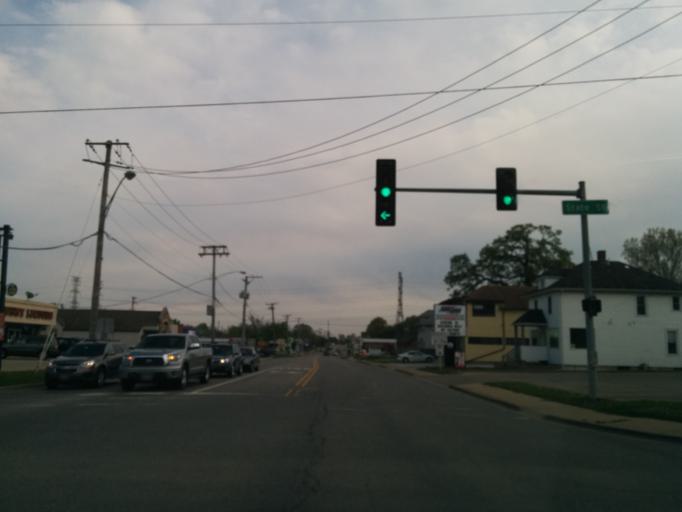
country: US
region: Illinois
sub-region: Kane County
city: North Aurora
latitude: 41.8062
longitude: -88.3271
